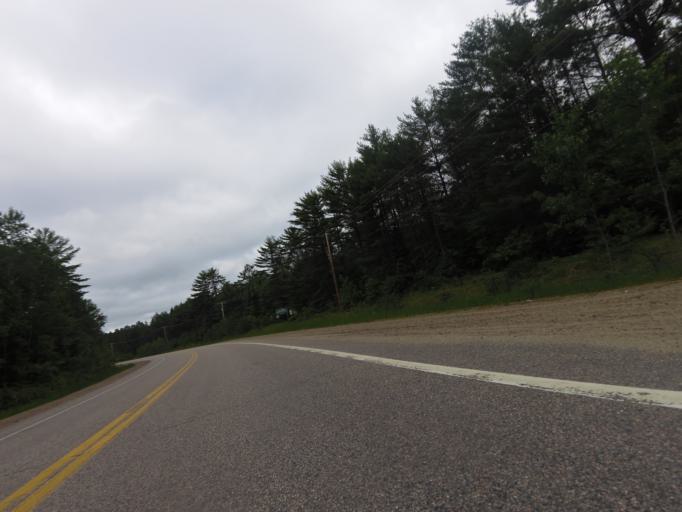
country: CA
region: Quebec
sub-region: Outaouais
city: Shawville
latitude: 45.8592
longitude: -76.4215
